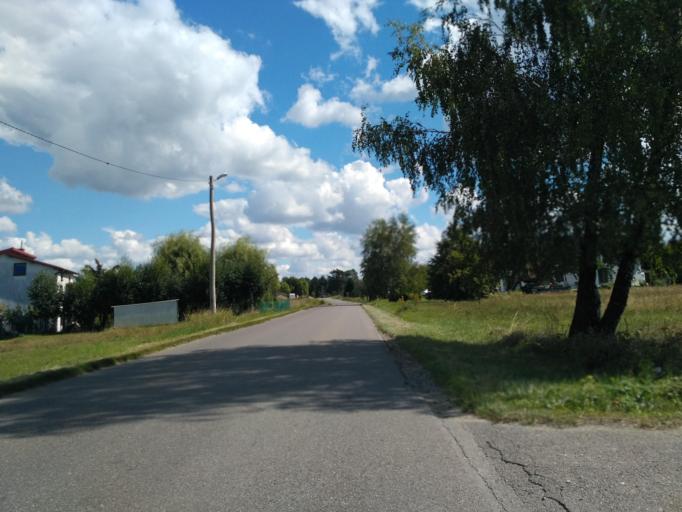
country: PL
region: Subcarpathian Voivodeship
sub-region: Powiat jasielski
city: Trzcinica
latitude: 49.7529
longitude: 21.4204
